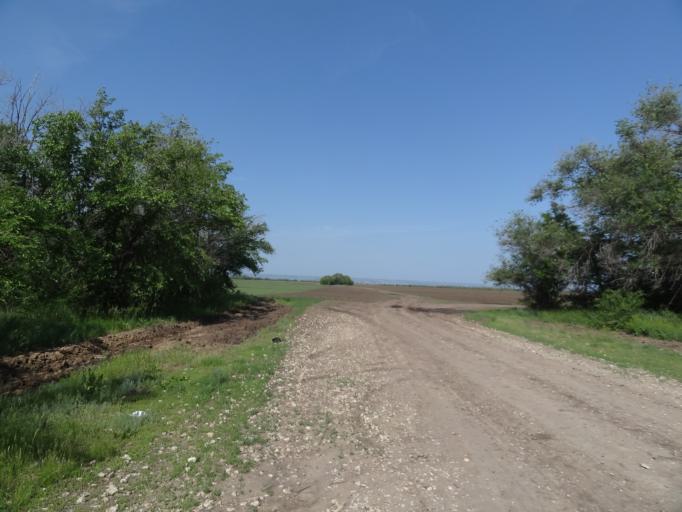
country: RU
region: Saratov
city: Privolzhskiy
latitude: 51.1505
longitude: 45.9617
